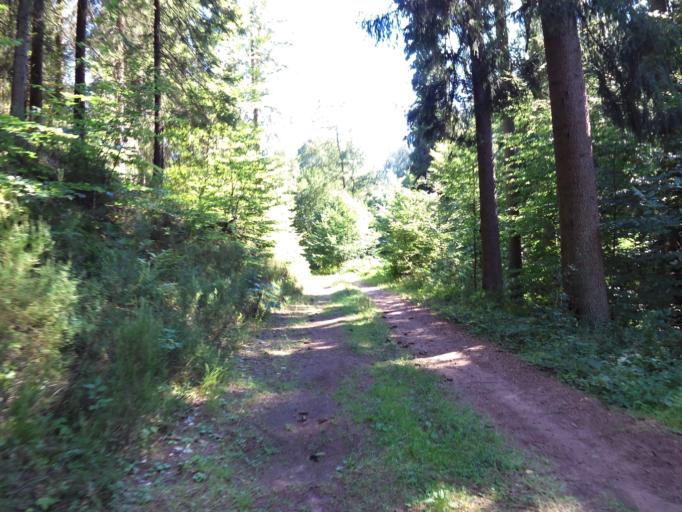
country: DE
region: Rheinland-Pfalz
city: Esthal
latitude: 49.3737
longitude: 7.9743
